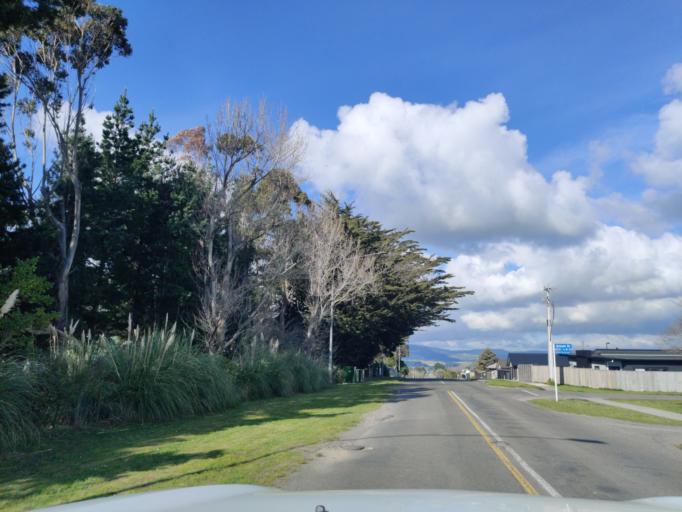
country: NZ
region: Manawatu-Wanganui
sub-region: Palmerston North City
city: Palmerston North
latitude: -40.3202
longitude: 175.6580
